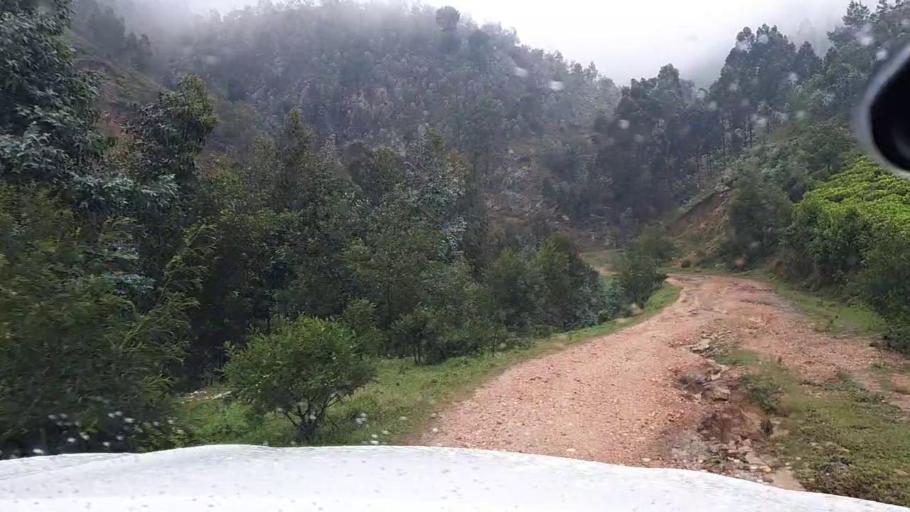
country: RW
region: Western Province
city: Kibuye
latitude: -2.1357
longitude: 29.4581
